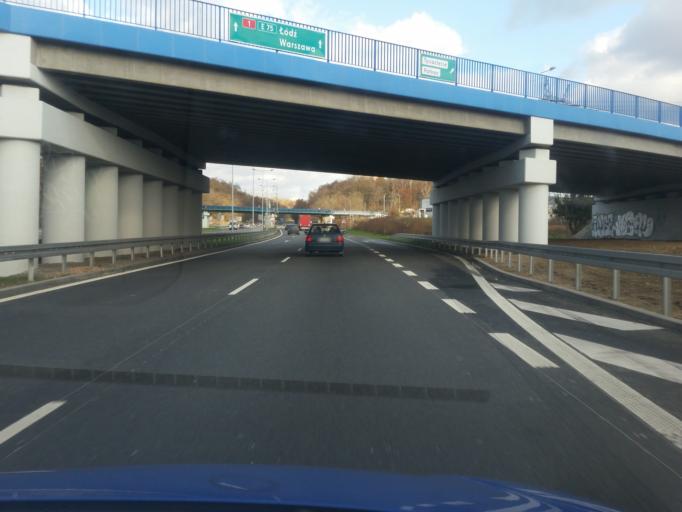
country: PL
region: Silesian Voivodeship
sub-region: Czestochowa
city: Czestochowa
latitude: 50.8303
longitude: 19.1455
